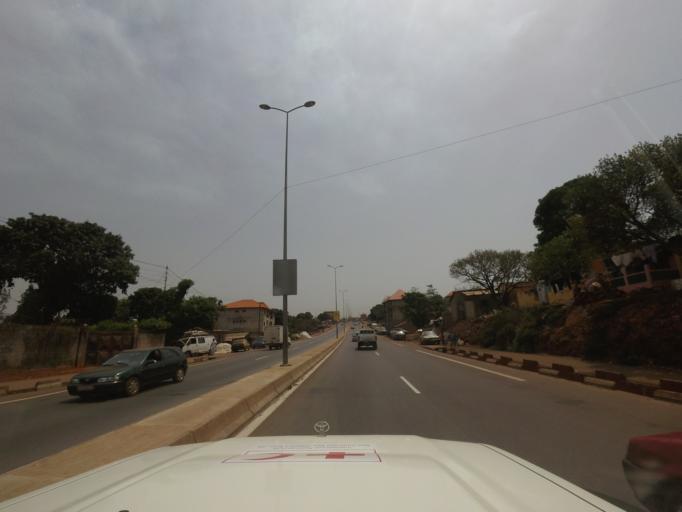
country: GN
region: Kindia
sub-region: Prefecture de Dubreka
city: Dubreka
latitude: 9.6935
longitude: -13.5069
